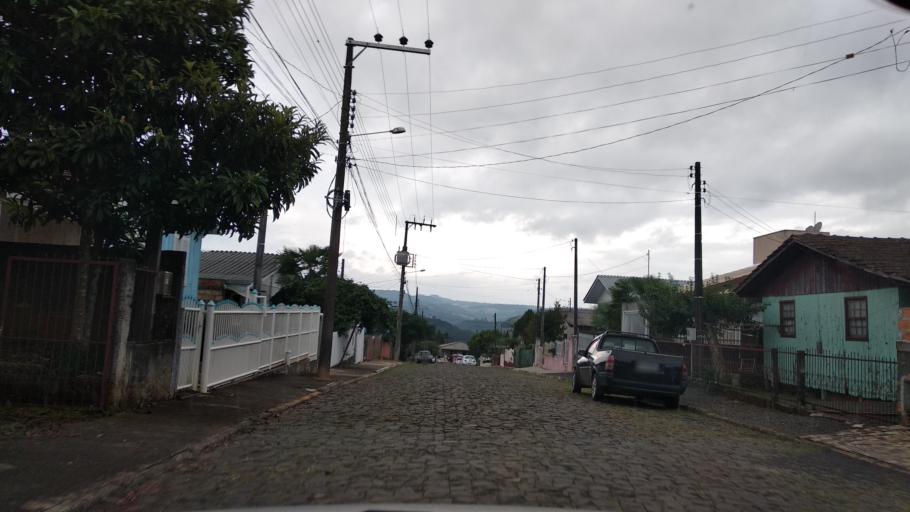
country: BR
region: Santa Catarina
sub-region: Videira
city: Videira
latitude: -26.9871
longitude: -51.1748
